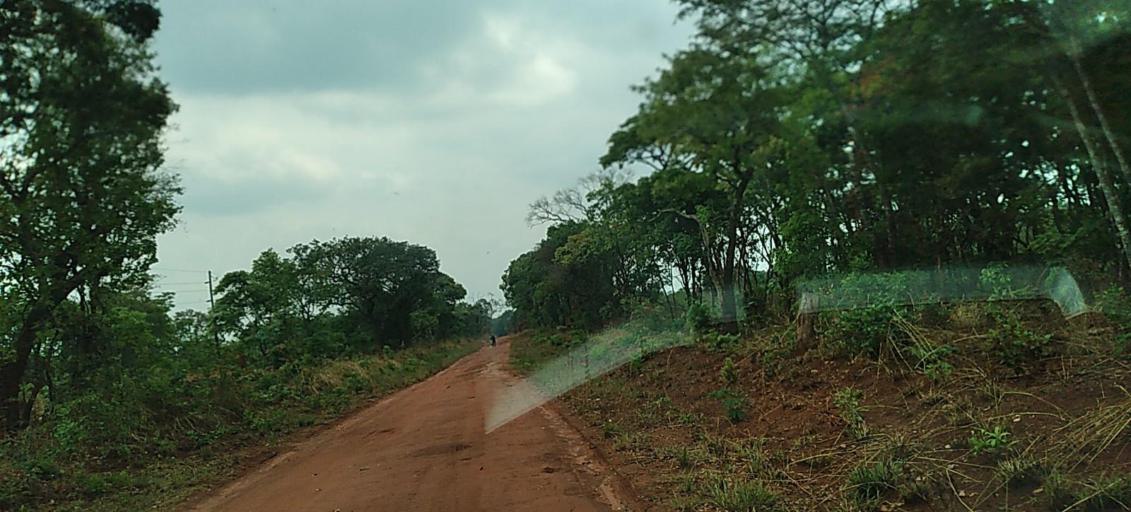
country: ZM
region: North-Western
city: Mwinilunga
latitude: -11.5462
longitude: 24.7772
